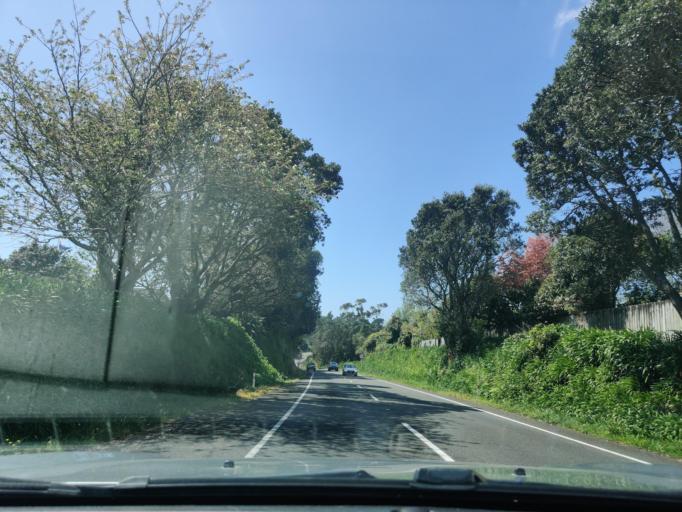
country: NZ
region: Taranaki
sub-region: New Plymouth District
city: New Plymouth
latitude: -39.1150
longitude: 173.9576
